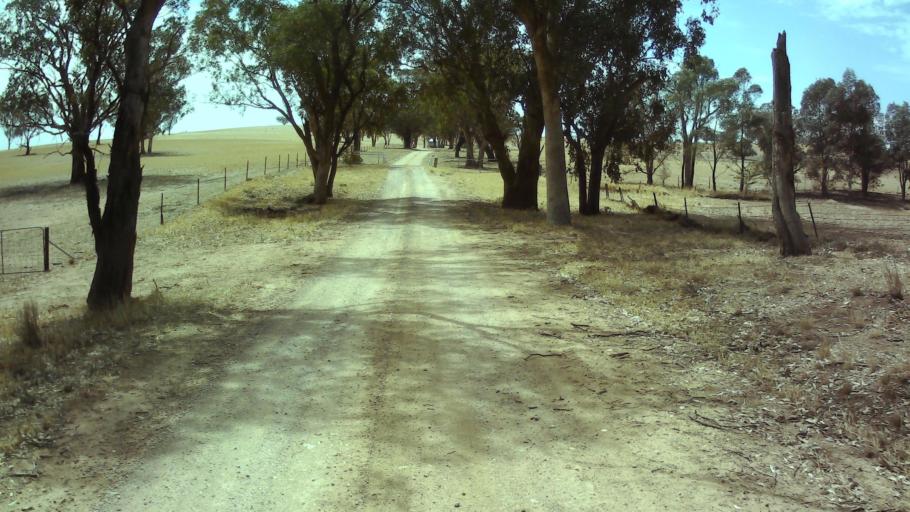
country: AU
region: New South Wales
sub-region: Cowra
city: Cowra
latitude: -33.9287
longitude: 148.4621
